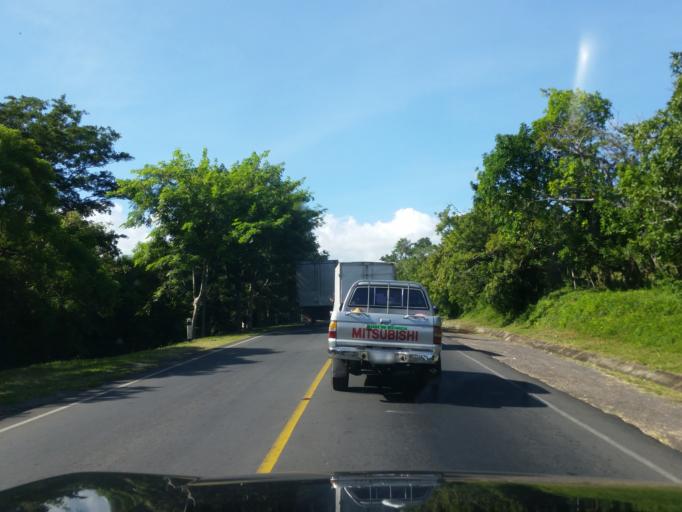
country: NI
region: Granada
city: Diria
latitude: 11.8935
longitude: -86.0626
